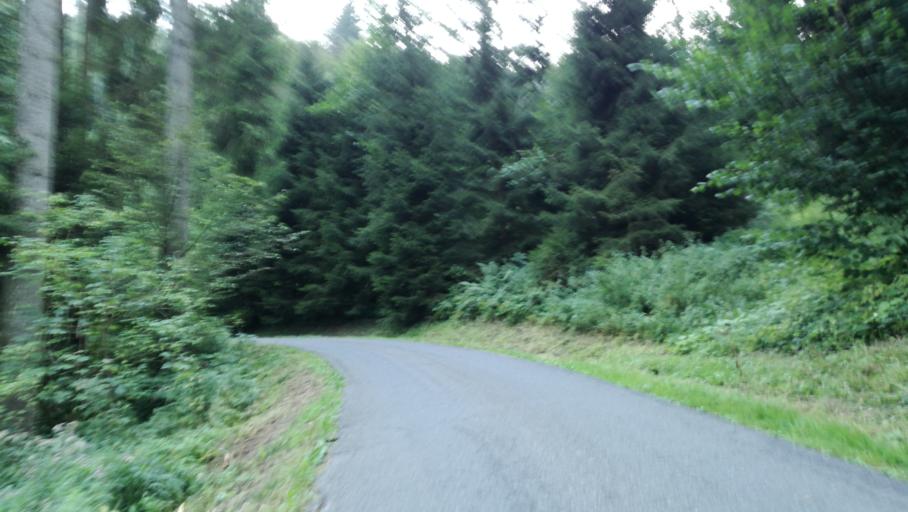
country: CH
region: Zug
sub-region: Zug
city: Zug
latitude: 47.1465
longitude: 8.5447
